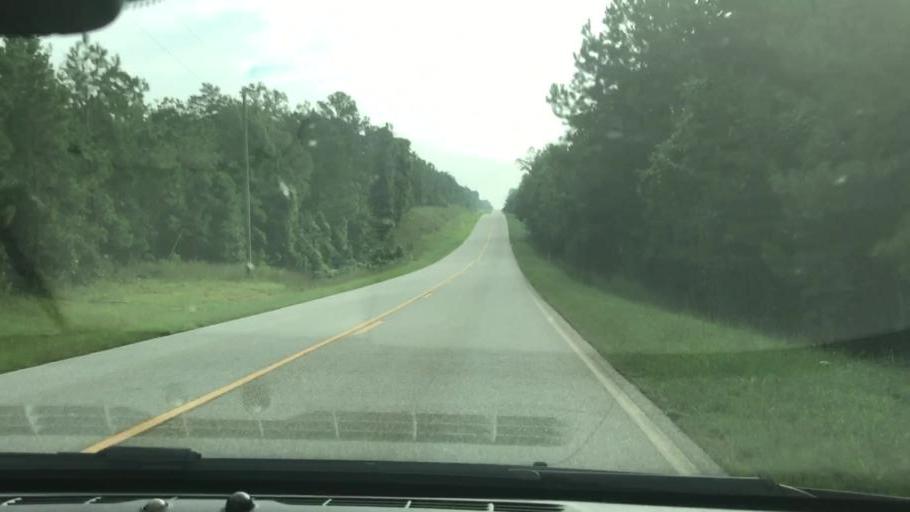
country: US
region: Georgia
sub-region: Stewart County
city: Lumpkin
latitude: 32.0188
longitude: -84.9262
